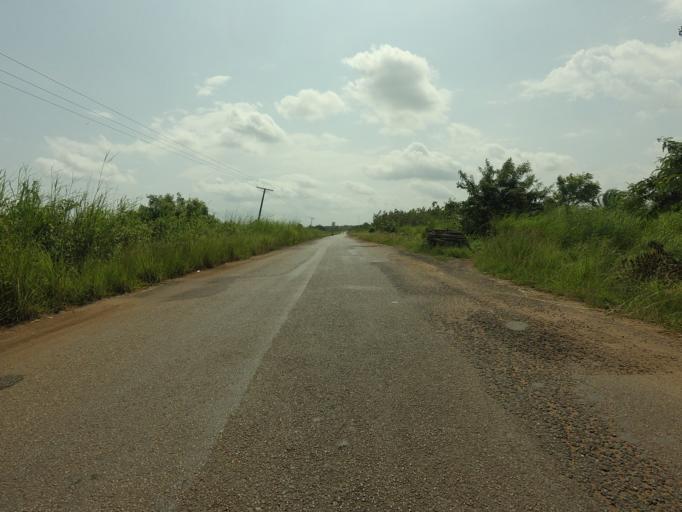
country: TG
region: Maritime
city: Lome
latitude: 6.2571
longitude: 0.9632
